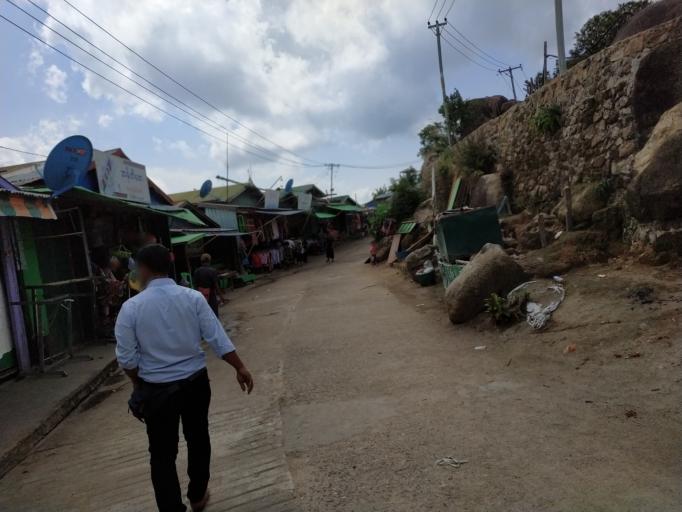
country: MM
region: Mon
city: Kyaikto
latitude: 17.4757
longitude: 97.1020
